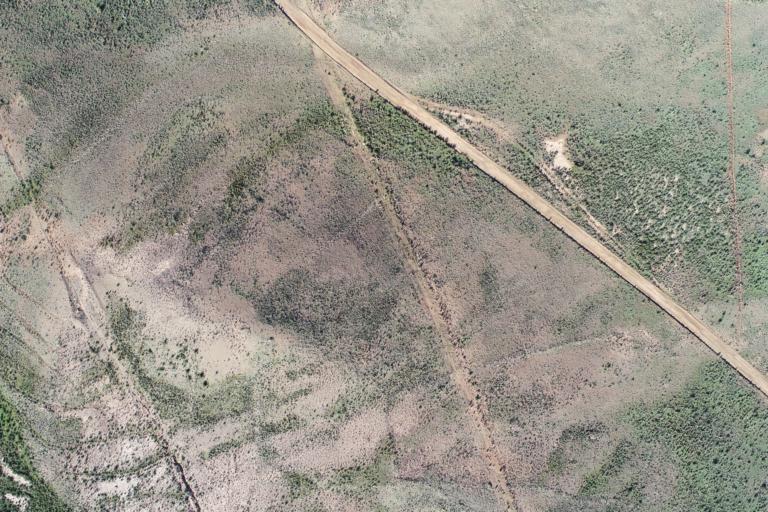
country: BO
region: La Paz
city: Curahuara de Carangas
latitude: -17.3040
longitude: -68.5043
